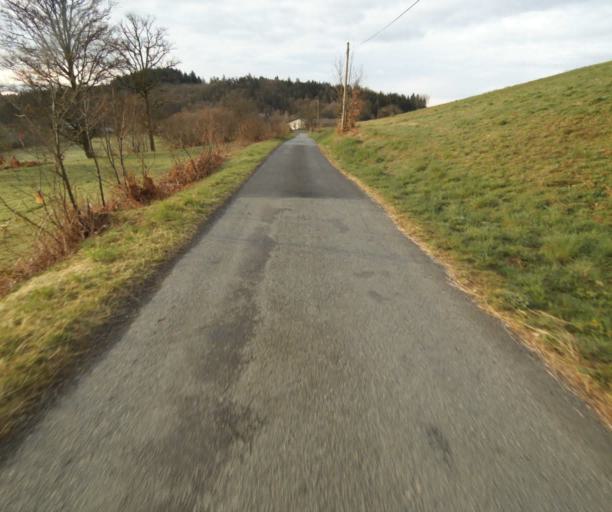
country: FR
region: Limousin
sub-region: Departement de la Correze
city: Correze
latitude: 45.3972
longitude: 1.8667
